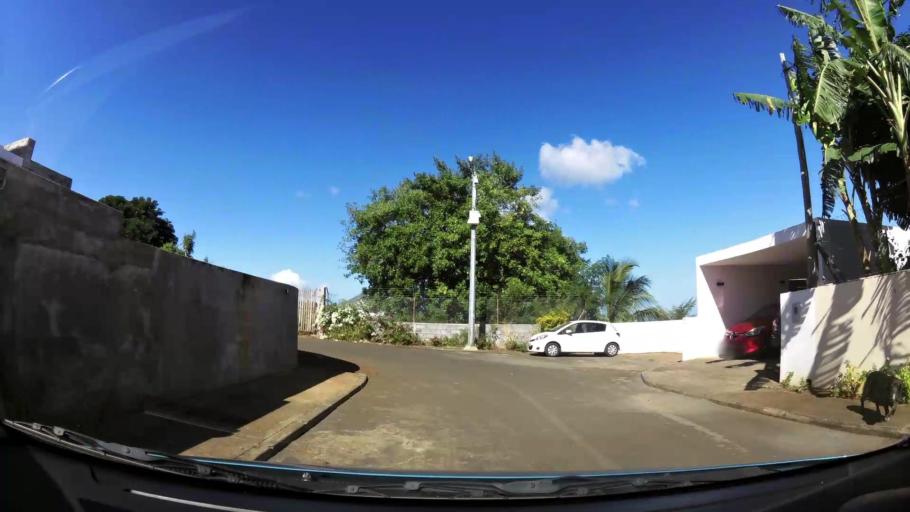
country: MU
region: Black River
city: Flic en Flac
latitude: -20.2799
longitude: 57.3765
